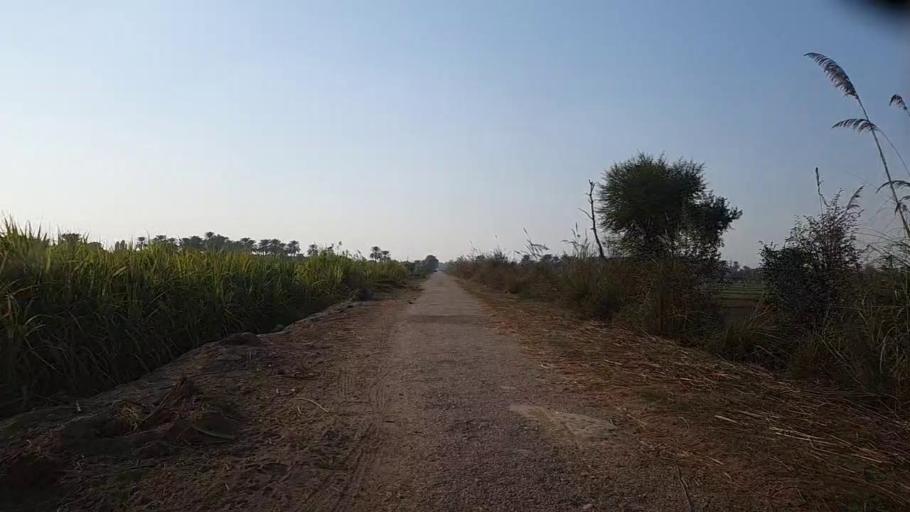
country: PK
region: Sindh
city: Ranipur
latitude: 27.2511
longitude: 68.5550
